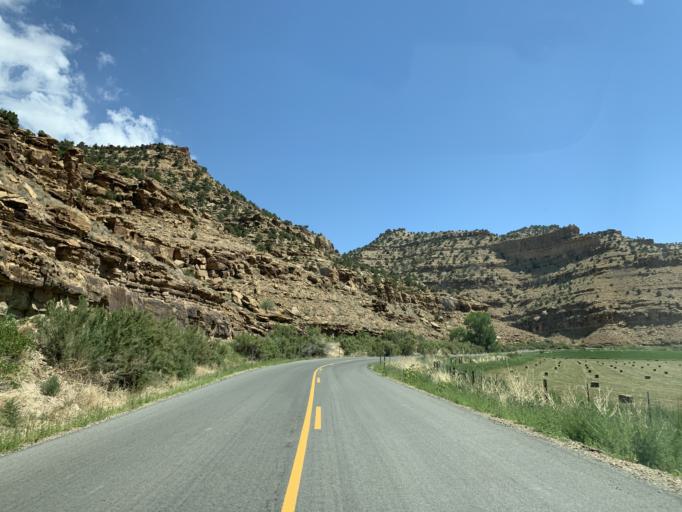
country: US
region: Utah
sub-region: Carbon County
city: East Carbon City
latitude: 39.8104
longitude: -110.2555
